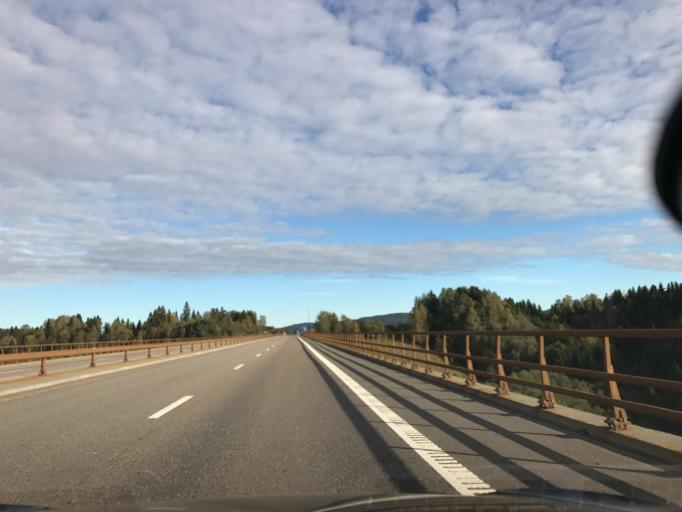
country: NO
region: Akershus
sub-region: Eidsvoll
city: Eidsvoll
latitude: 60.3746
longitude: 11.2072
